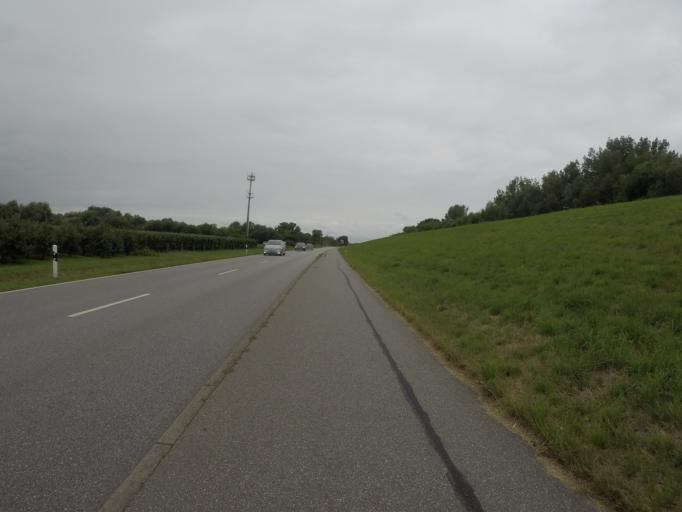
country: DE
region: Lower Saxony
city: Neu Wulmstorf
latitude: 53.5365
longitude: 9.7854
